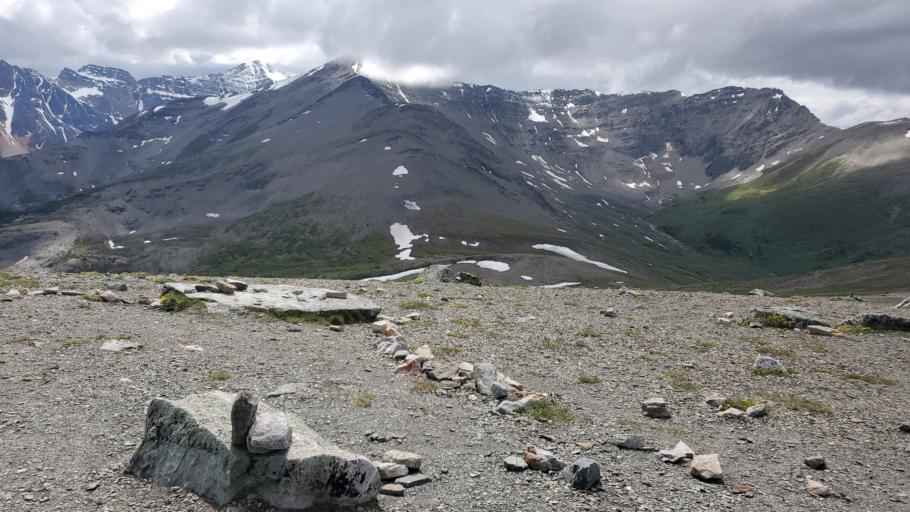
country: CA
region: Alberta
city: Jasper Park Lodge
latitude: 52.8270
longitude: -118.1337
